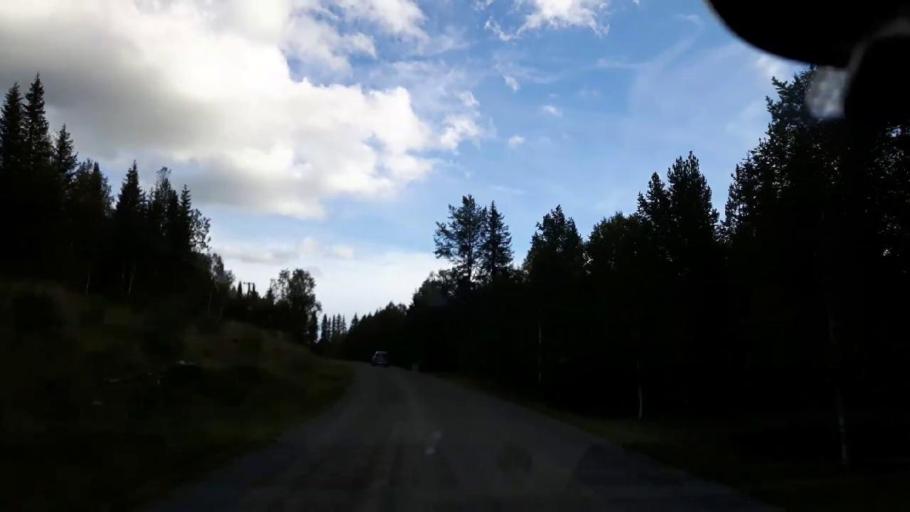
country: SE
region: Jaemtland
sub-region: Ragunda Kommun
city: Hammarstrand
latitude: 63.4165
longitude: 16.0778
